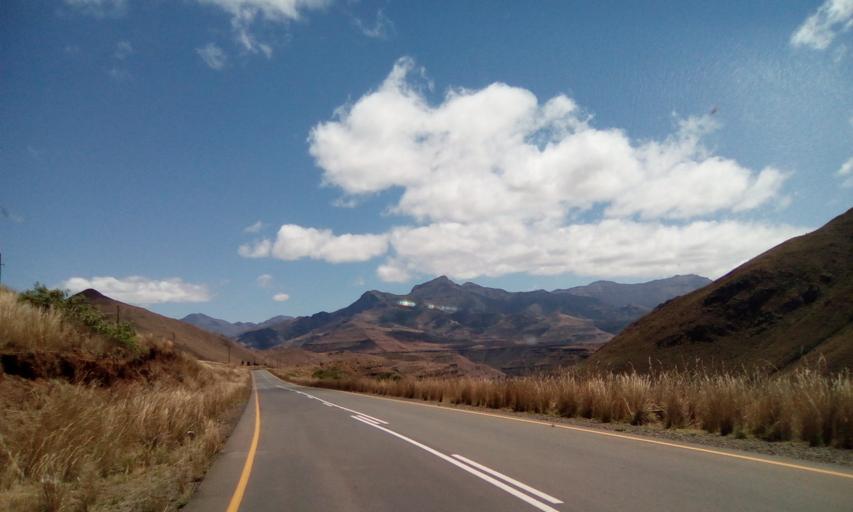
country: LS
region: Qacha's Nek
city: Qacha's Nek
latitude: -30.0842
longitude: 28.6317
